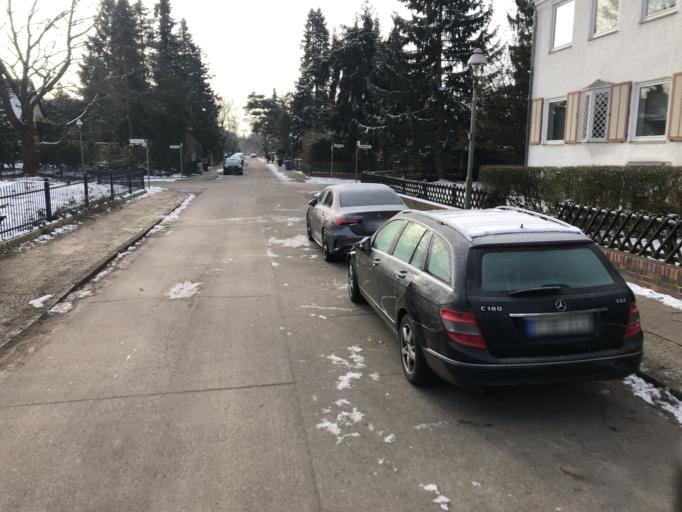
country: DE
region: Berlin
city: Hermsdorf
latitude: 52.6264
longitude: 13.3080
